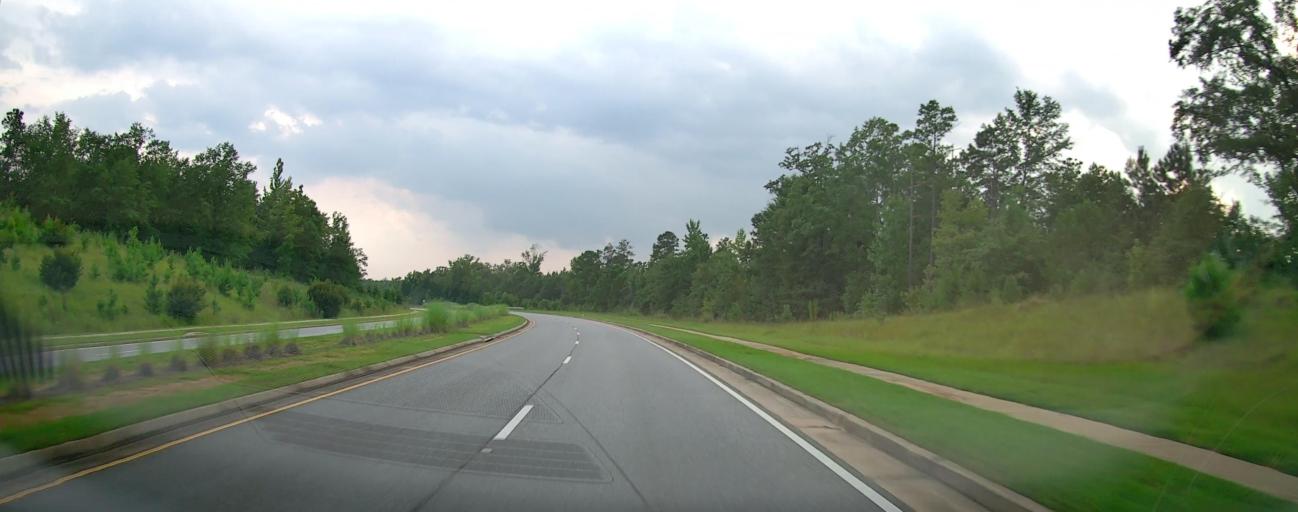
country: US
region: Georgia
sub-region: Muscogee County
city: Columbus
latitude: 32.5111
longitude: -84.8523
